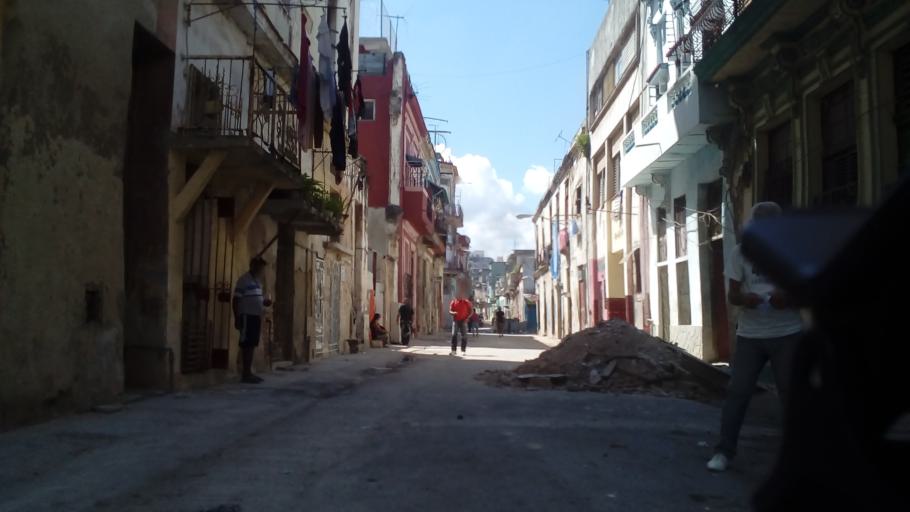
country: CU
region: La Habana
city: Centro Habana
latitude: 23.1424
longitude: -82.3611
